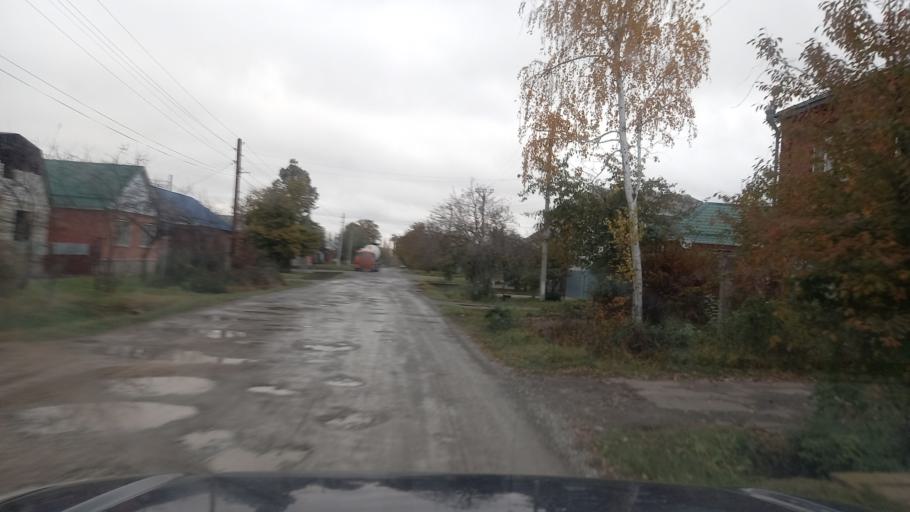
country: RU
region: Adygeya
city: Maykop
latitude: 44.6163
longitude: 40.1282
